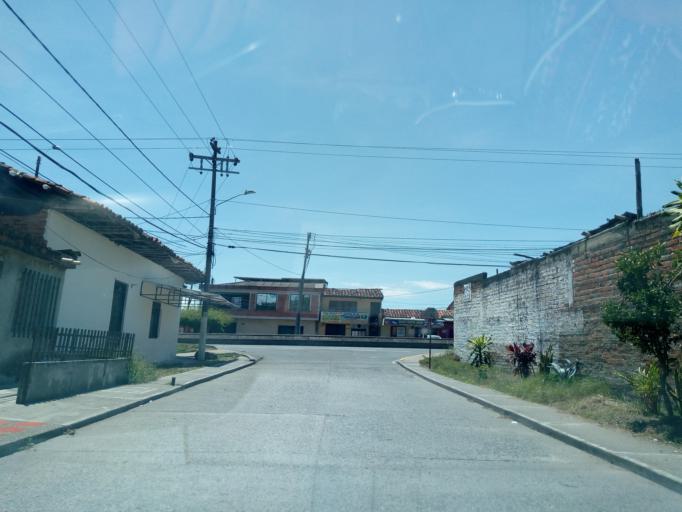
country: CO
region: Valle del Cauca
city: Cartago
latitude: 4.7321
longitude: -75.9062
